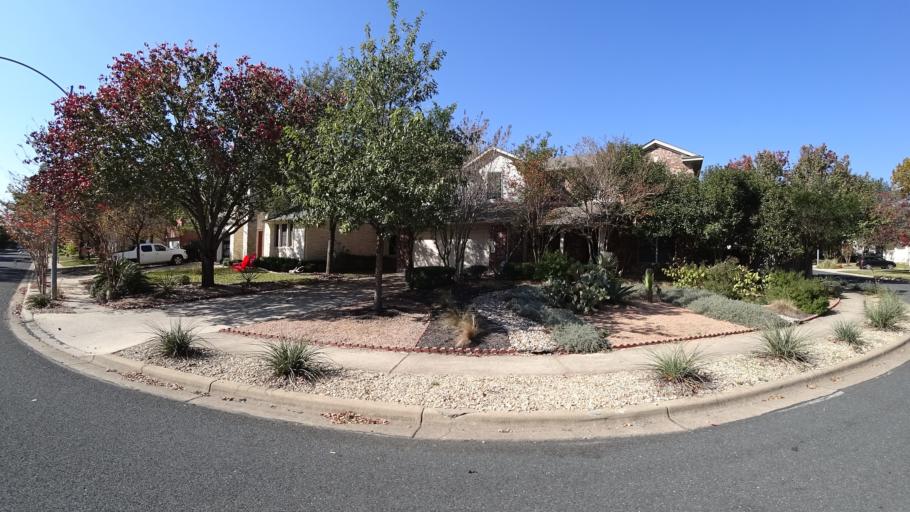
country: US
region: Texas
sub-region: Travis County
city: Barton Creek
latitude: 30.2298
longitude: -97.8670
